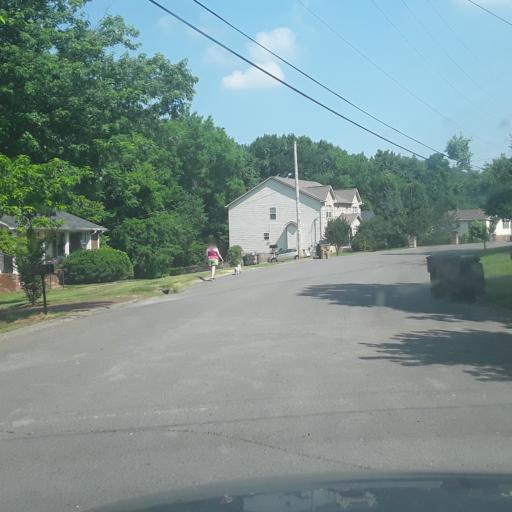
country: US
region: Tennessee
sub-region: Williamson County
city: Brentwood Estates
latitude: 36.0359
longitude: -86.7099
